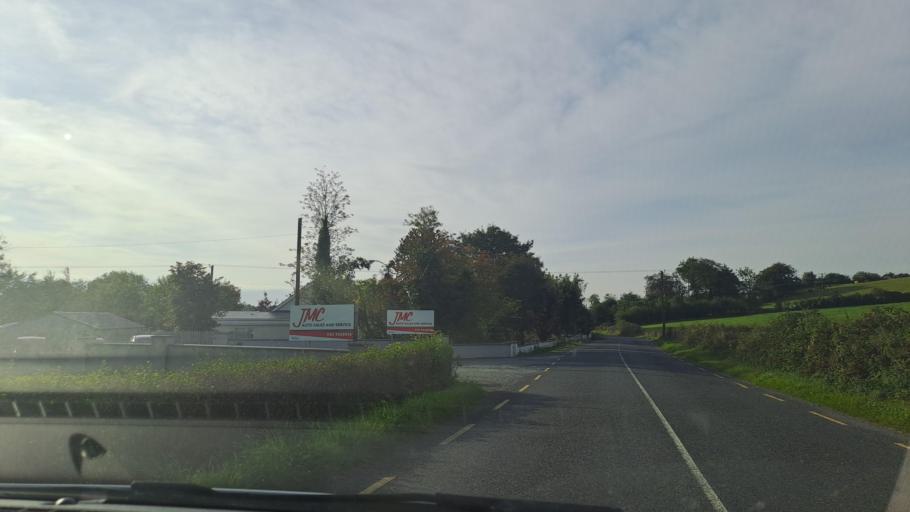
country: IE
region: Ulster
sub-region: An Cabhan
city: Kingscourt
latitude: 53.9489
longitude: -6.8396
